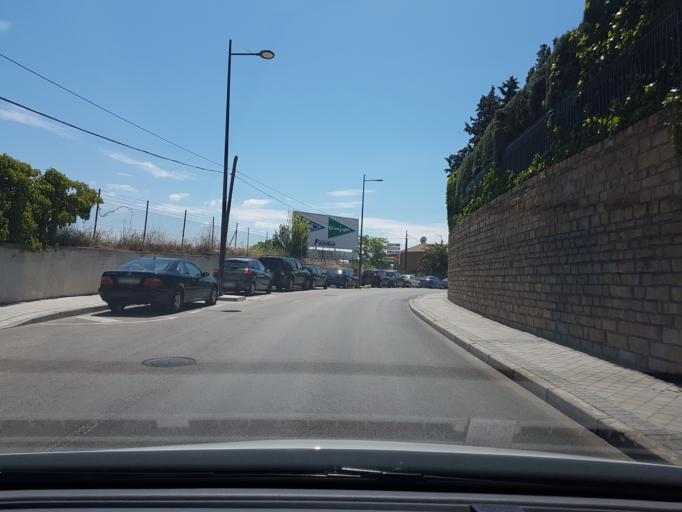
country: ES
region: Madrid
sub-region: Provincia de Madrid
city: Pozuelo de Alarcon
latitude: 40.4329
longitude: -3.8117
